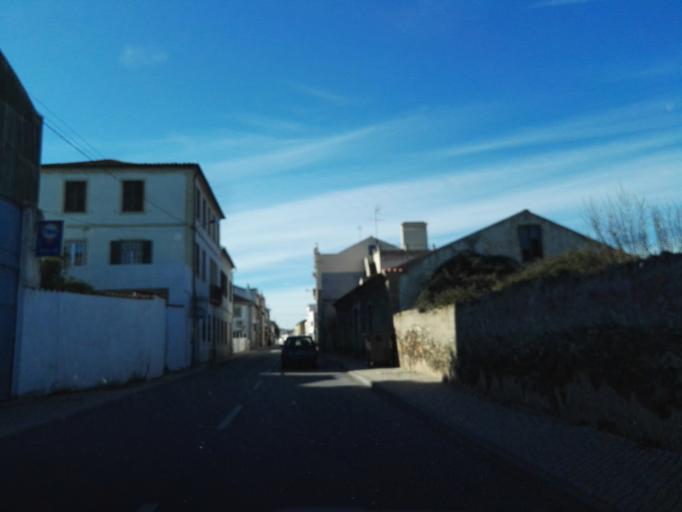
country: PT
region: Santarem
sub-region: Macao
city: Macao
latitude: 39.4649
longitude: -8.0440
